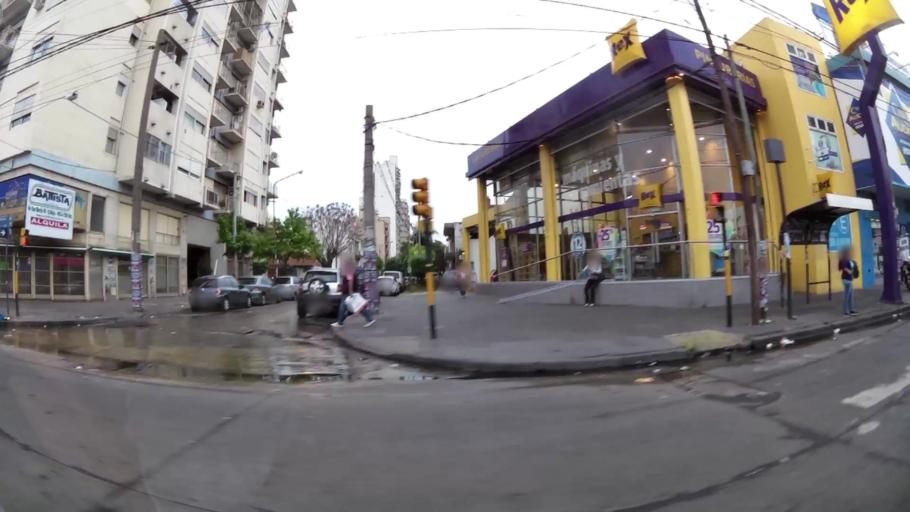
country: AR
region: Buenos Aires
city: San Justo
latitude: -34.6416
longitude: -58.5703
